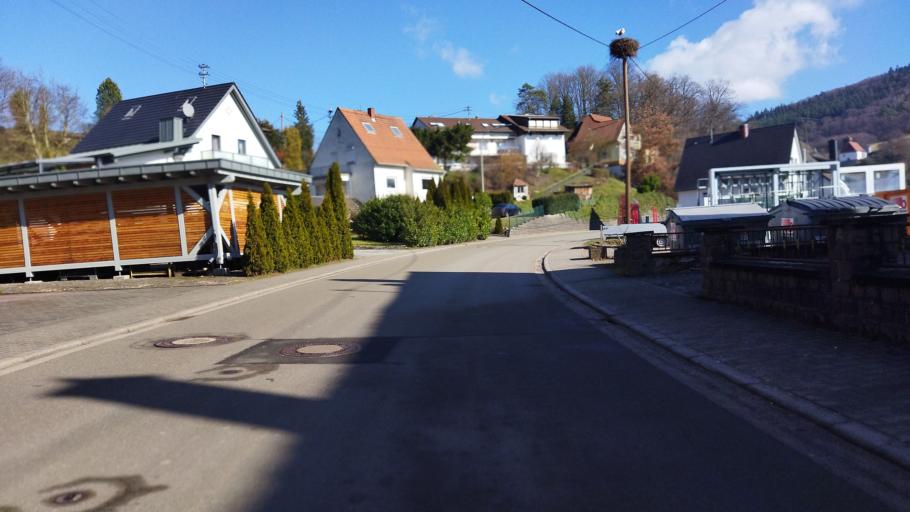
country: DE
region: Rheinland-Pfalz
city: Etschberg
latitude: 49.5166
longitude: 7.4437
